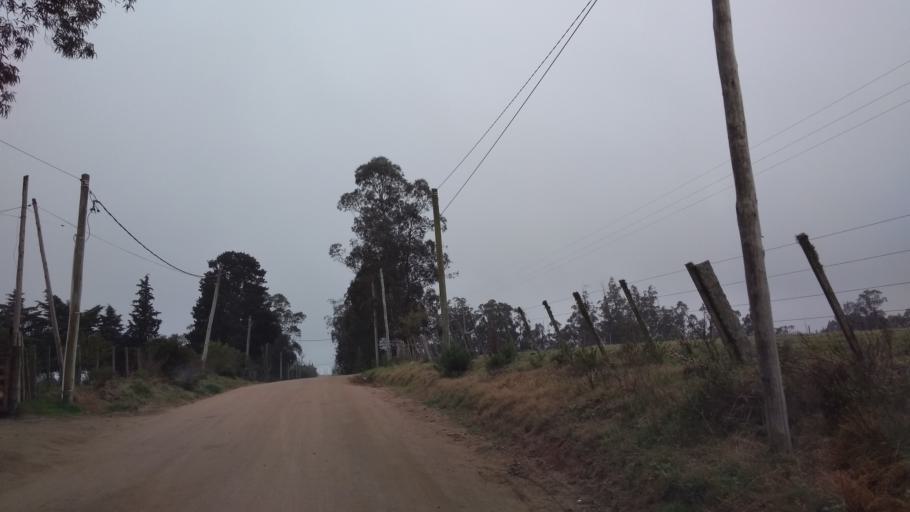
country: UY
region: Florida
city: Florida
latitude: -34.0797
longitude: -56.2025
